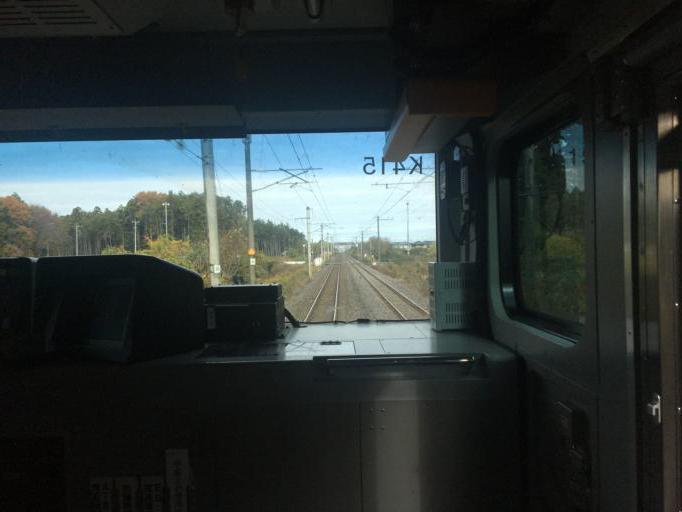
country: JP
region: Ibaraki
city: Ishioka
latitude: 36.2375
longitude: 140.2894
